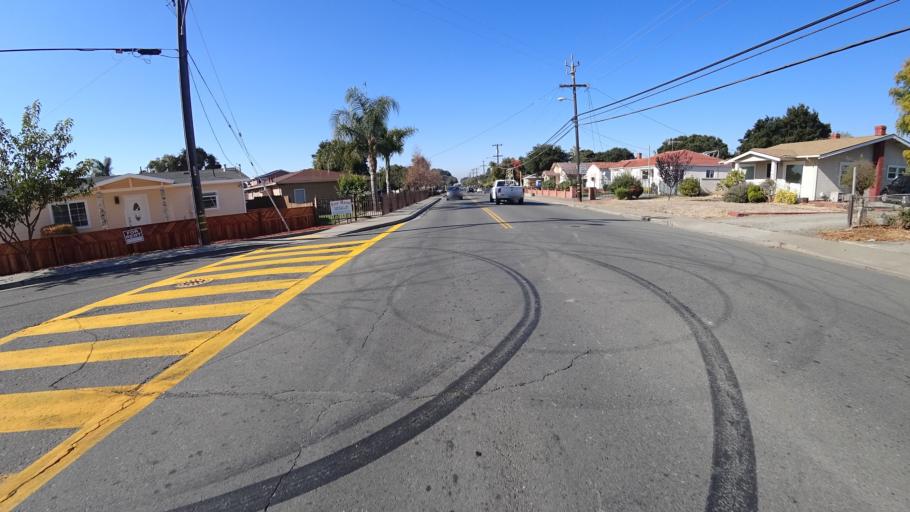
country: US
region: California
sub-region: Alameda County
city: Union City
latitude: 37.6059
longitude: -122.0234
